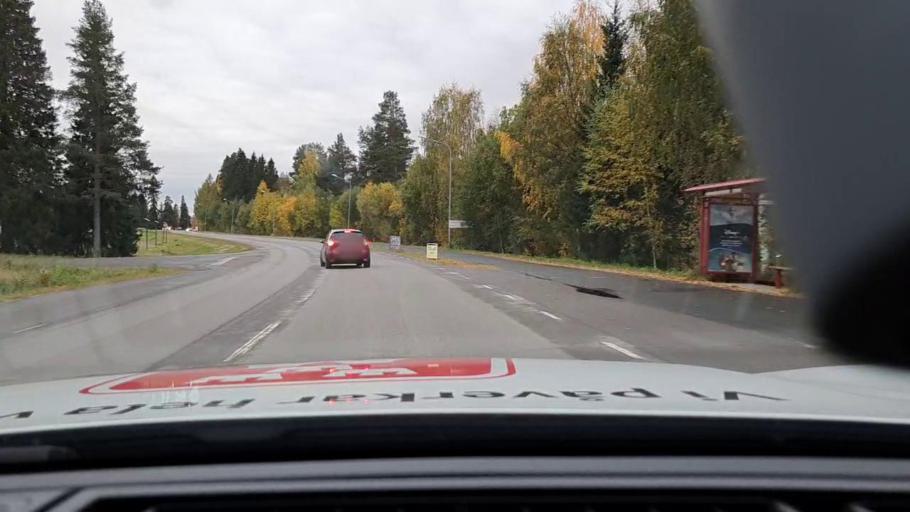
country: SE
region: Norrbotten
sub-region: Bodens Kommun
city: Boden
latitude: 65.8127
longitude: 21.6775
